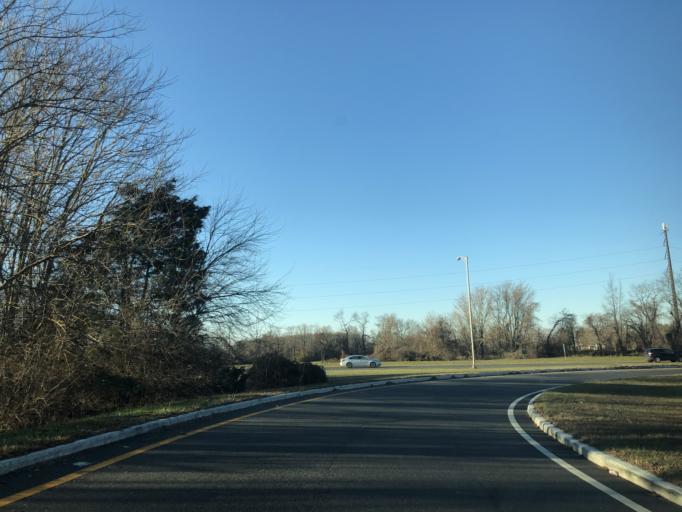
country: US
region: New Jersey
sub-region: Salem County
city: Carneys Point
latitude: 39.7072
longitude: -75.4469
